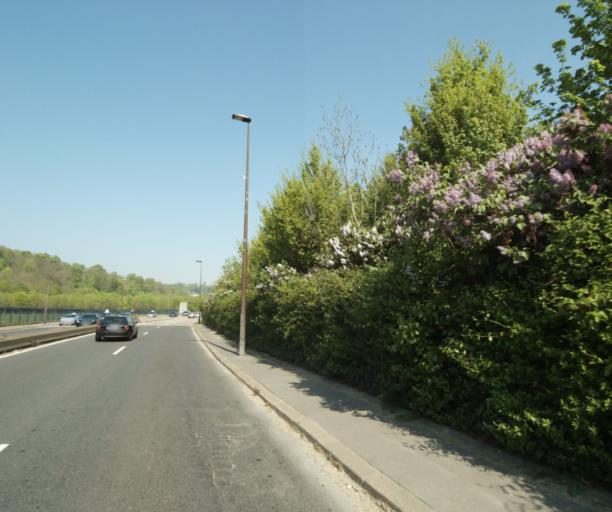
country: FR
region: Ile-de-France
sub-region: Departement des Hauts-de-Seine
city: Sevres
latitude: 48.8301
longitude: 2.2235
